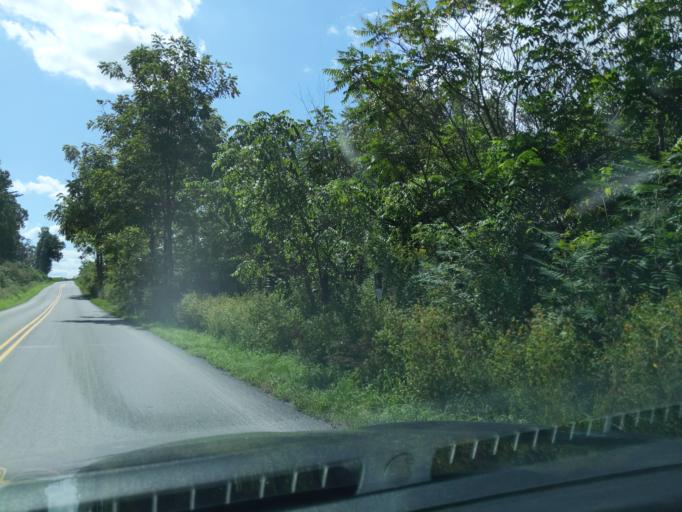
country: US
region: Pennsylvania
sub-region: Blair County
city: Tyrone
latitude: 40.6490
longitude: -78.2140
